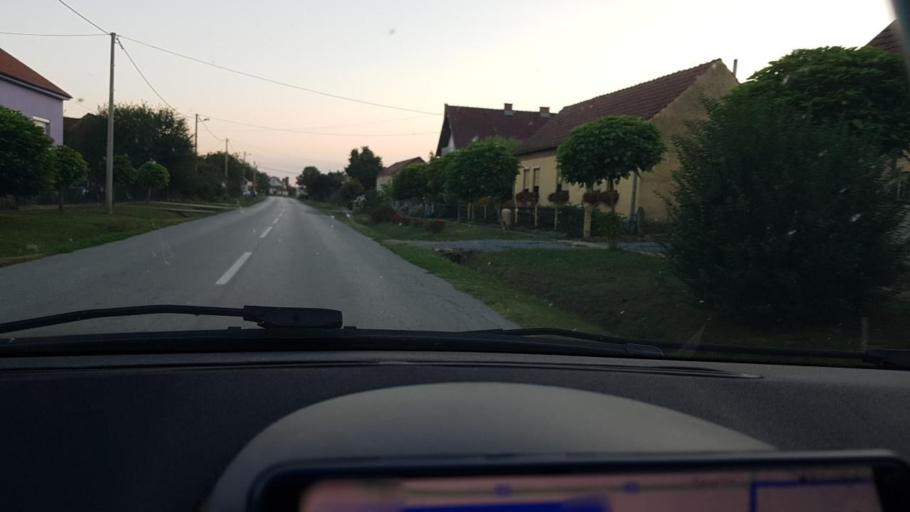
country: HR
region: Bjelovarsko-Bilogorska
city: Zdralovi
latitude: 45.8378
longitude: 16.9632
